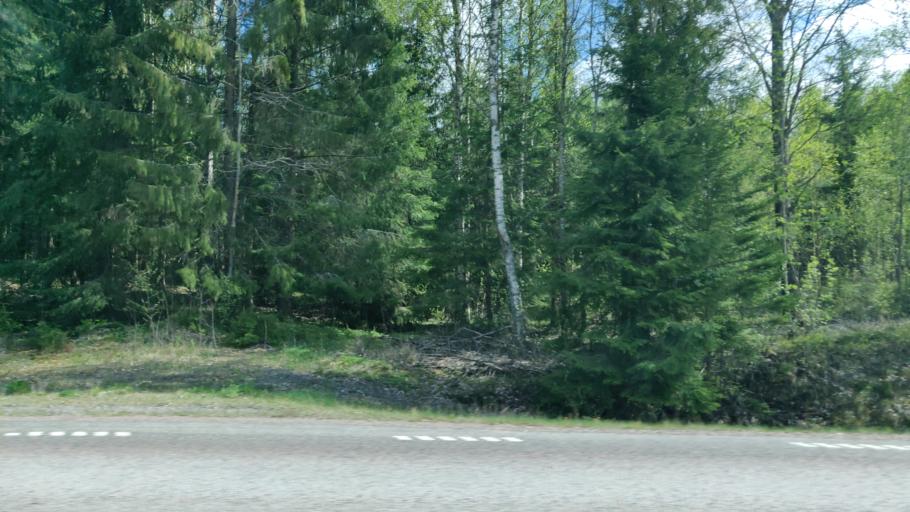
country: SE
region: Vaermland
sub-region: Karlstads Kommun
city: Molkom
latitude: 59.5734
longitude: 13.6677
